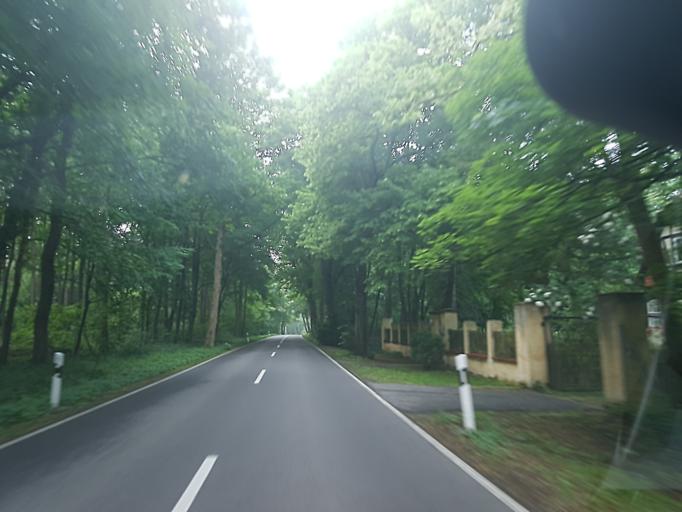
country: DE
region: Saxony-Anhalt
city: Klieken
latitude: 51.9981
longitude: 12.3655
